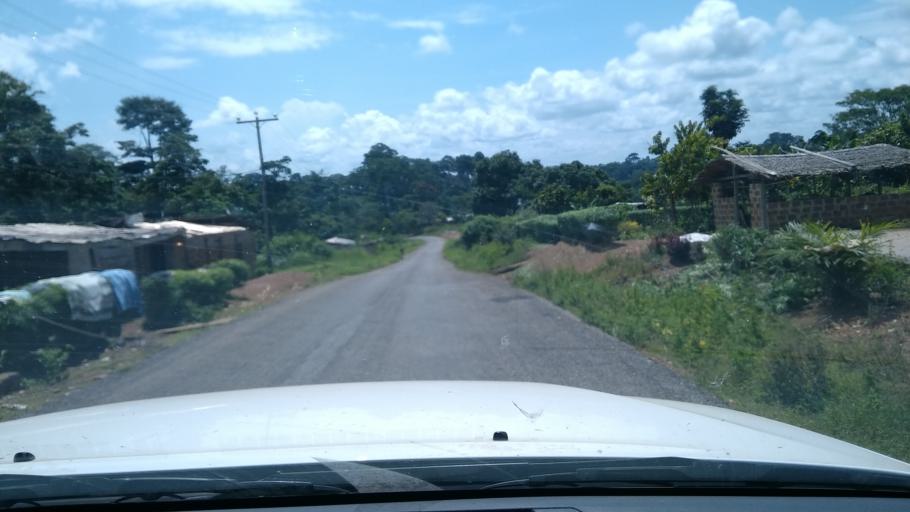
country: CM
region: Centre
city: Evodoula
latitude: 4.1456
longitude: 11.2746
